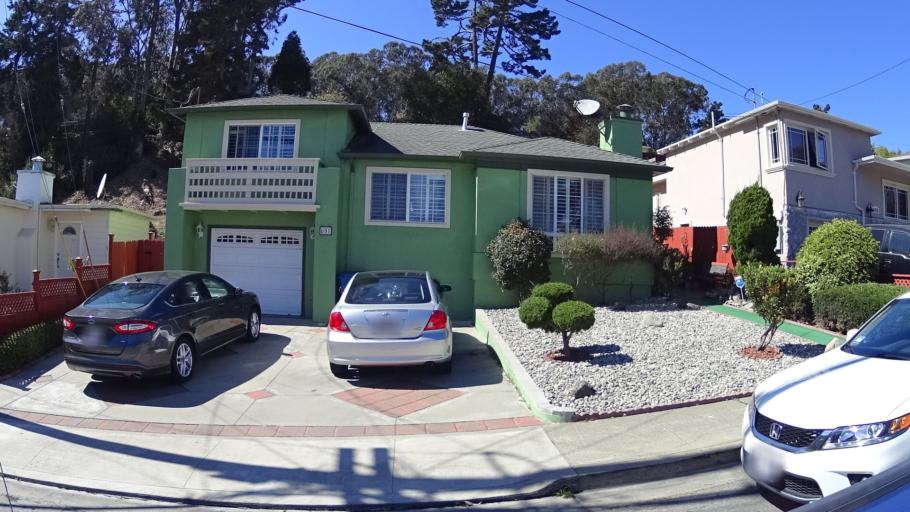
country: US
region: California
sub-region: San Mateo County
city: Broadmoor
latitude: 37.6887
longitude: -122.4826
